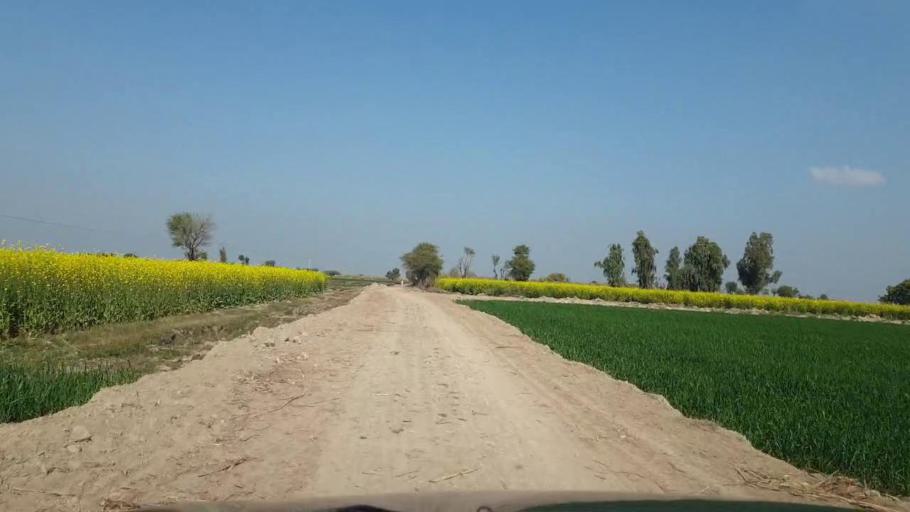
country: PK
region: Sindh
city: Sinjhoro
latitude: 26.0540
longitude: 68.7294
